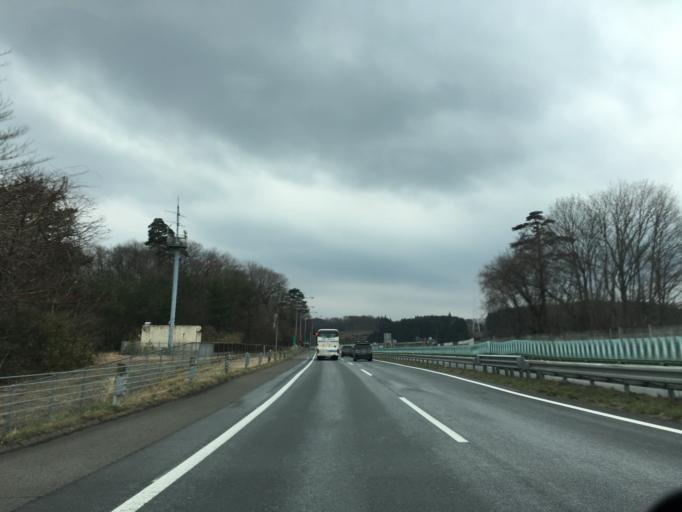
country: JP
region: Tochigi
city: Kuroiso
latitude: 37.1062
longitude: 140.1439
